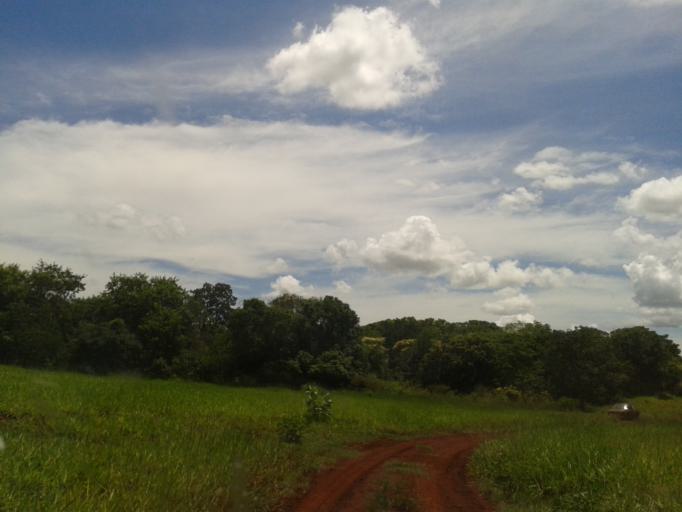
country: BR
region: Minas Gerais
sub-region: Capinopolis
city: Capinopolis
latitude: -18.7739
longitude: -49.8128
